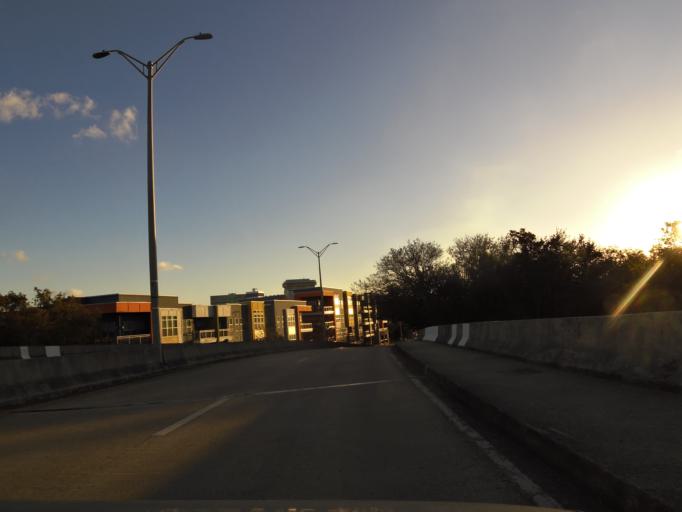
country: US
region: Florida
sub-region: Duval County
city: Jacksonville
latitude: 30.3266
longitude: -81.6712
